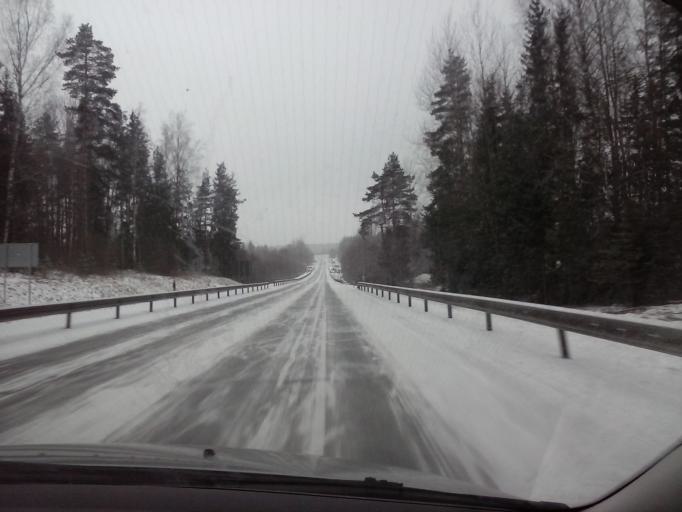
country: EE
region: Valgamaa
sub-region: Valga linn
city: Valga
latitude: 57.8539
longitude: 26.1359
